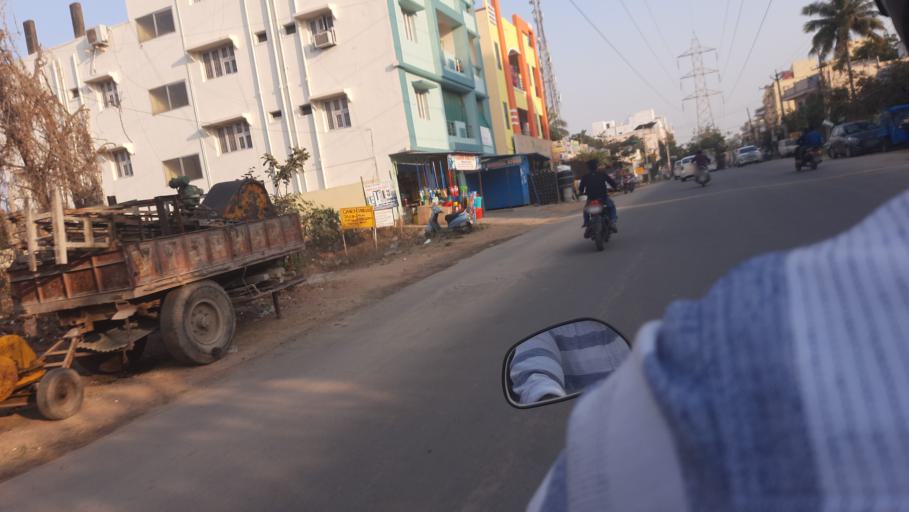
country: IN
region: Telangana
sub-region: Rangareddi
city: Secunderabad
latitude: 17.4941
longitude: 78.5457
